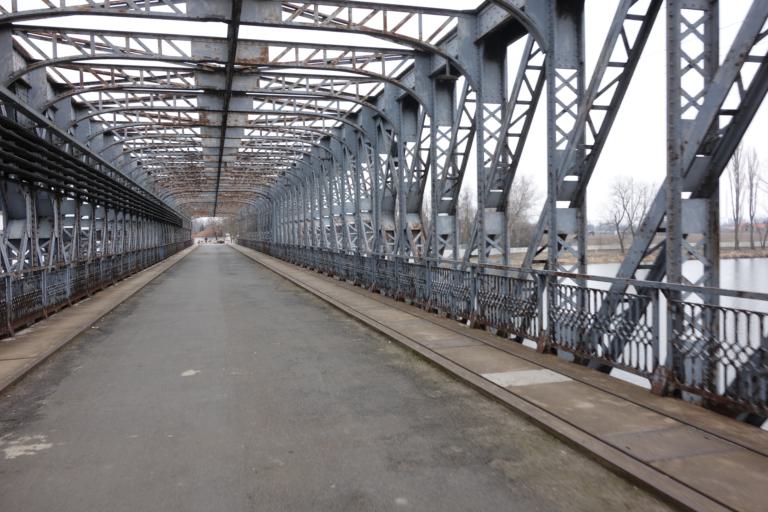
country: CZ
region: Central Bohemia
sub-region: Okres Melnik
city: Veltrusy
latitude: 50.2759
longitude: 14.3125
